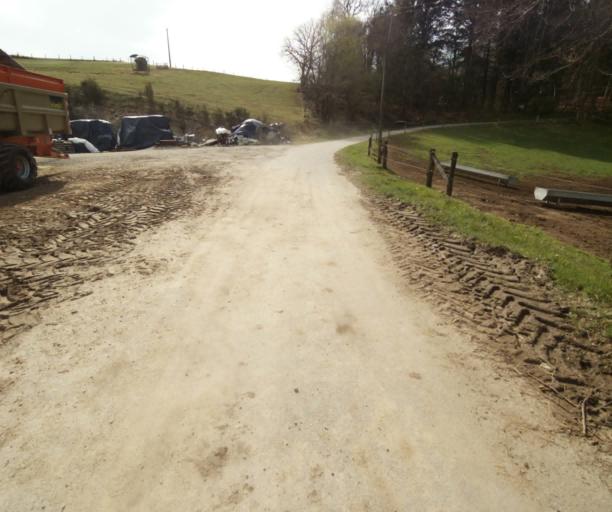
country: FR
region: Limousin
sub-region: Departement de la Correze
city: Correze
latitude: 45.3636
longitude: 1.9081
